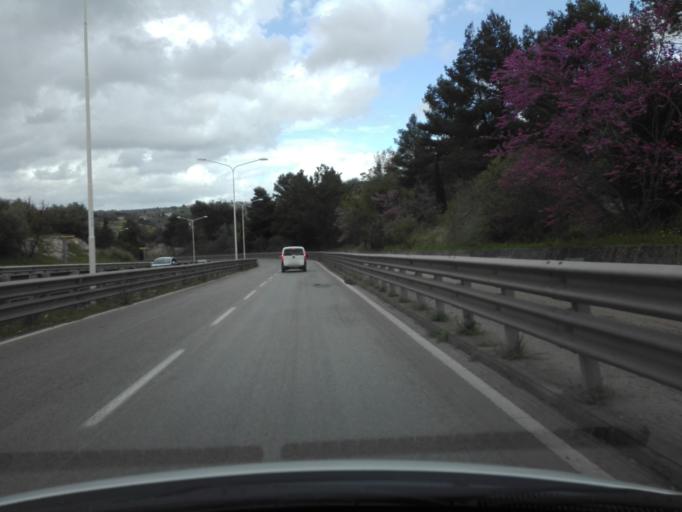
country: IT
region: Sardinia
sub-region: Provincia di Sassari
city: Sassari
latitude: 40.7296
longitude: 8.5761
